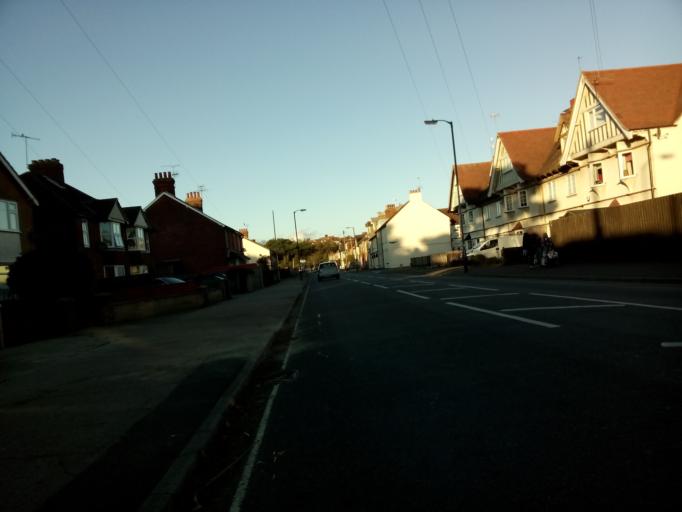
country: GB
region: England
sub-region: Suffolk
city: Felixstowe
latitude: 51.9560
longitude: 1.3390
